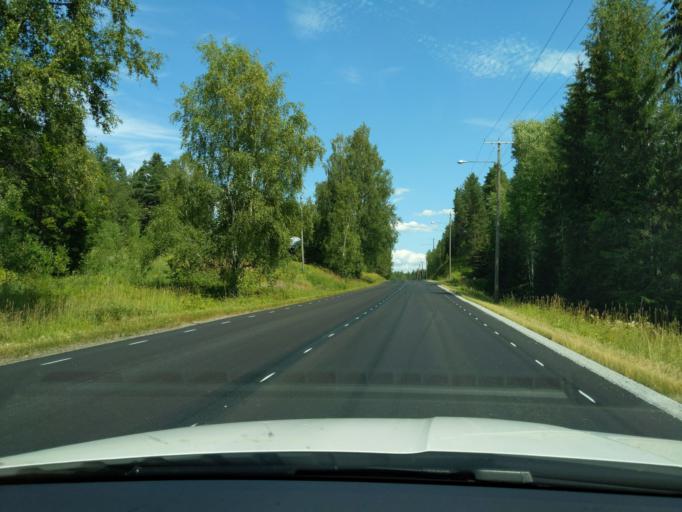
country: FI
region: Paijanne Tavastia
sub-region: Lahti
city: Lahti
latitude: 61.0395
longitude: 25.7552
